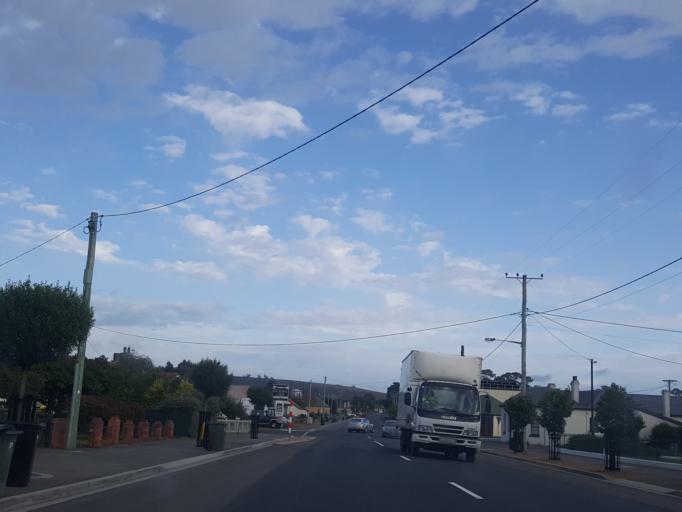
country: AU
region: Tasmania
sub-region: Northern Midlands
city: Perth
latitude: -41.5755
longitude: 147.1730
